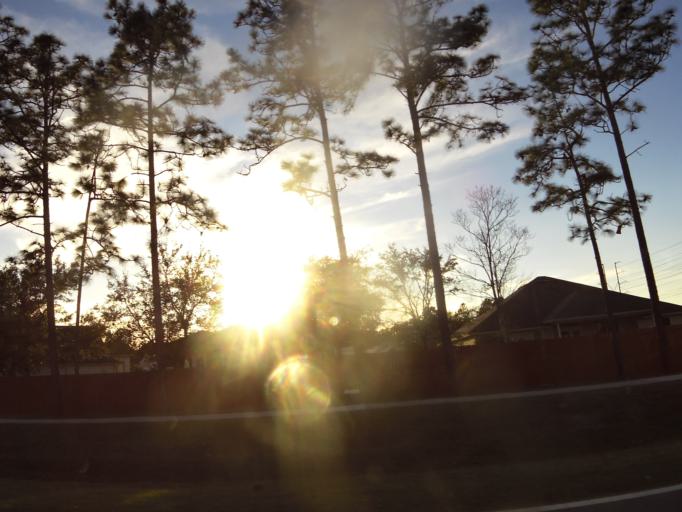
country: US
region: Florida
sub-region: Duval County
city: Jacksonville
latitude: 30.4540
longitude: -81.6693
